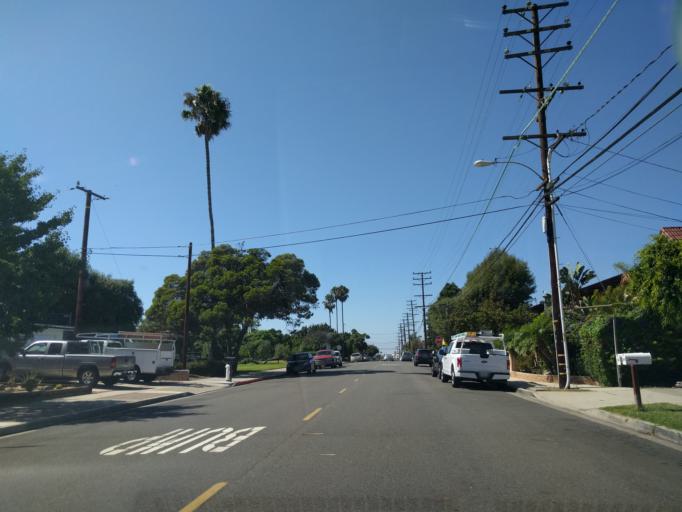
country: US
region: California
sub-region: Orange County
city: Costa Mesa
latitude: 33.6311
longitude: -117.9192
